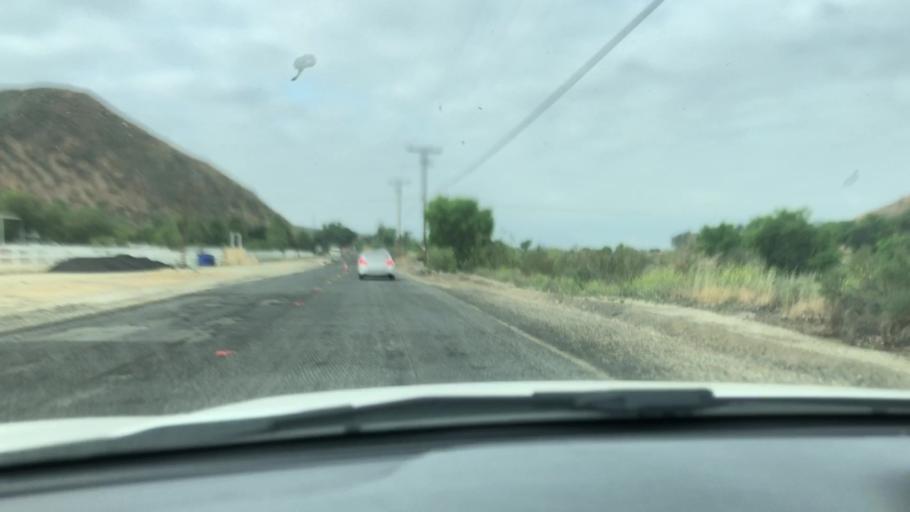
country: US
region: California
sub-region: Los Angeles County
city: Castaic
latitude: 34.4889
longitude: -118.5424
